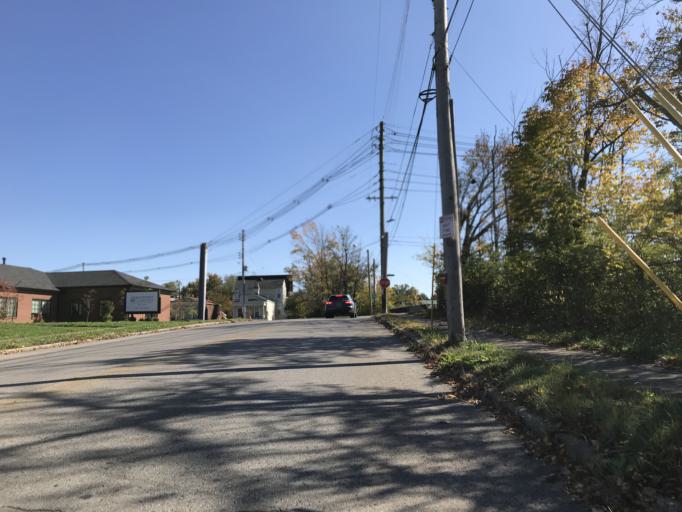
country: US
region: Indiana
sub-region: Clark County
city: Jeffersonville
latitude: 38.2528
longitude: -85.7177
